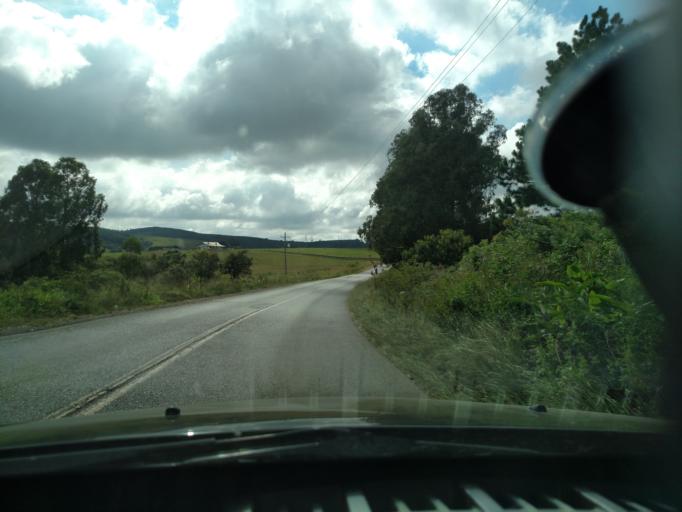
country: BR
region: Santa Catarina
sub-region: Lages
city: Lages
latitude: -27.8150
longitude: -50.2777
